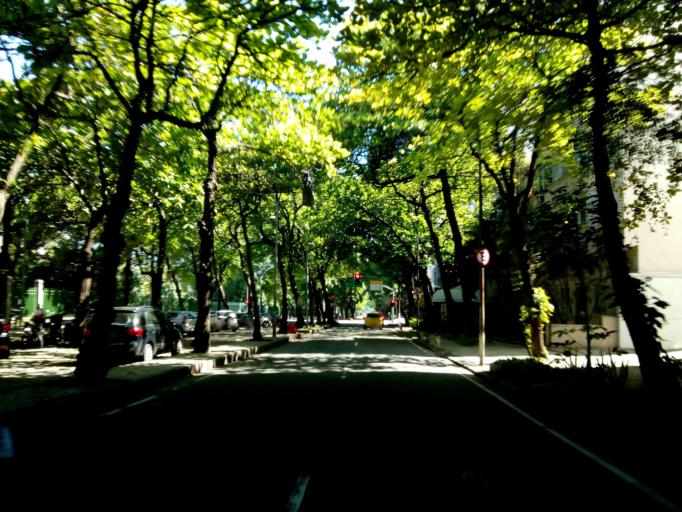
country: BR
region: Rio de Janeiro
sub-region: Rio De Janeiro
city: Rio de Janeiro
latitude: -22.9847
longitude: -43.2149
